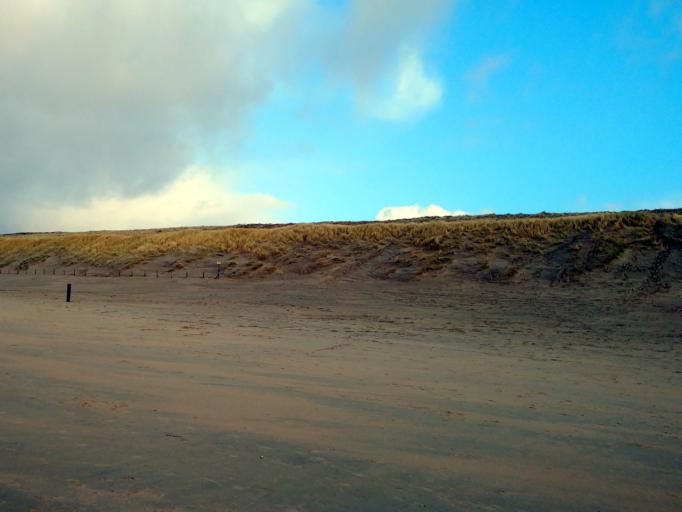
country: NL
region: South Holland
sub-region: Gemeente Noordwijkerhout
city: Noordwijkerhout
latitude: 52.3055
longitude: 4.4770
